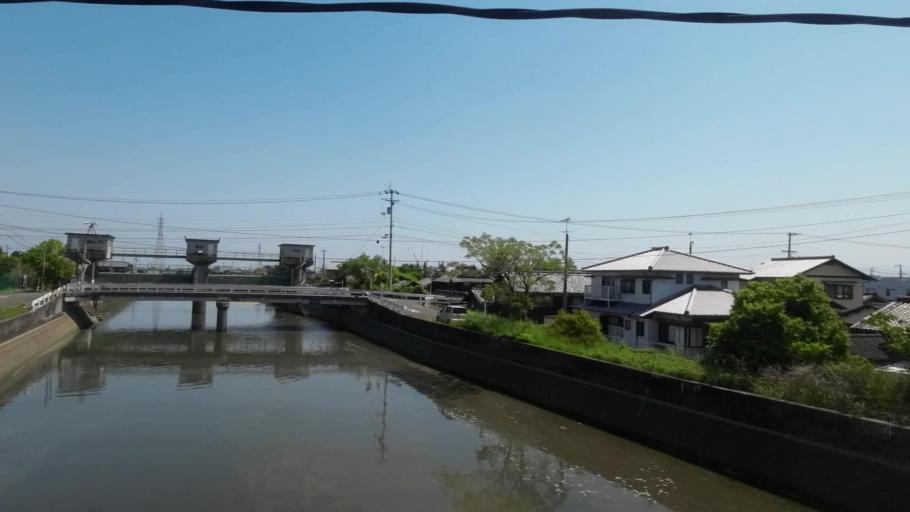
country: JP
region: Ehime
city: Saijo
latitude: 33.9378
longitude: 133.0784
